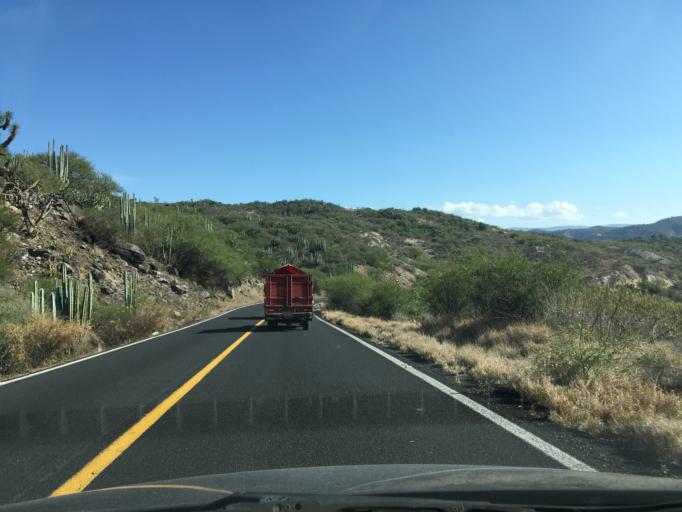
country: MX
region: Hidalgo
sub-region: San Agustin Metzquititlan
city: Mezquititlan
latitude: 20.4589
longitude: -98.6789
